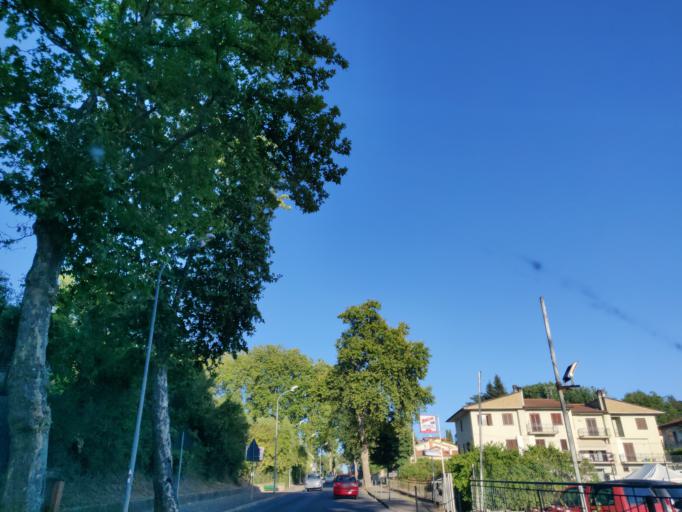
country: IT
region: Latium
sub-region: Provincia di Viterbo
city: Acquapendente
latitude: 42.7419
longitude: 11.8732
